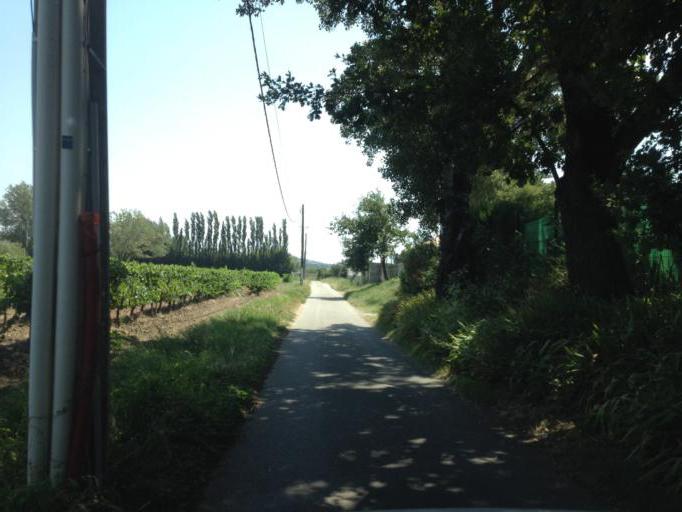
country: FR
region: Provence-Alpes-Cote d'Azur
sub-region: Departement du Vaucluse
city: Bedarrides
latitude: 44.0533
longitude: 4.8930
